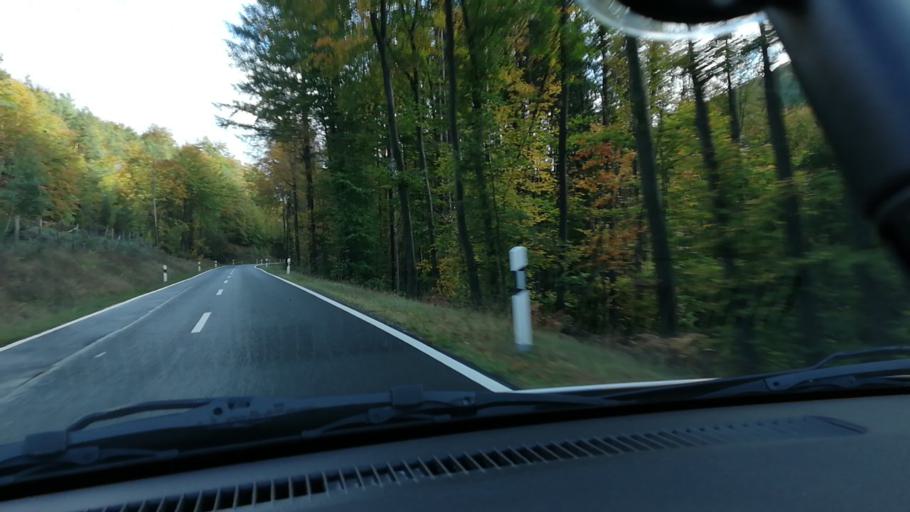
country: DE
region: Bavaria
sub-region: Regierungsbezirk Unterfranken
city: Neuhutten
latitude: 49.9943
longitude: 9.4513
